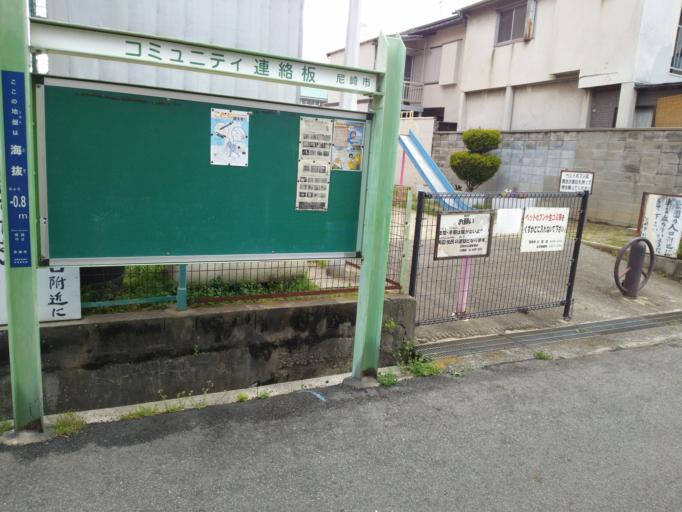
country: JP
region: Hyogo
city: Amagasaki
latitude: 34.7199
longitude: 135.4070
